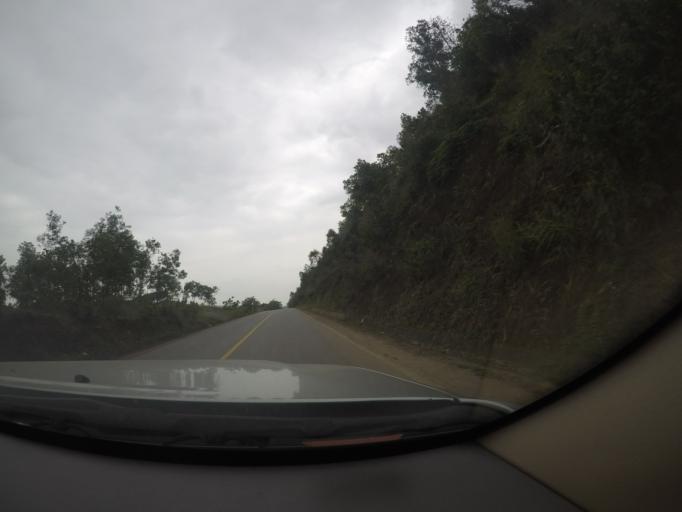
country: VN
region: Quang Binh
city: Hoan Lao
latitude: 17.5996
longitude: 106.4177
